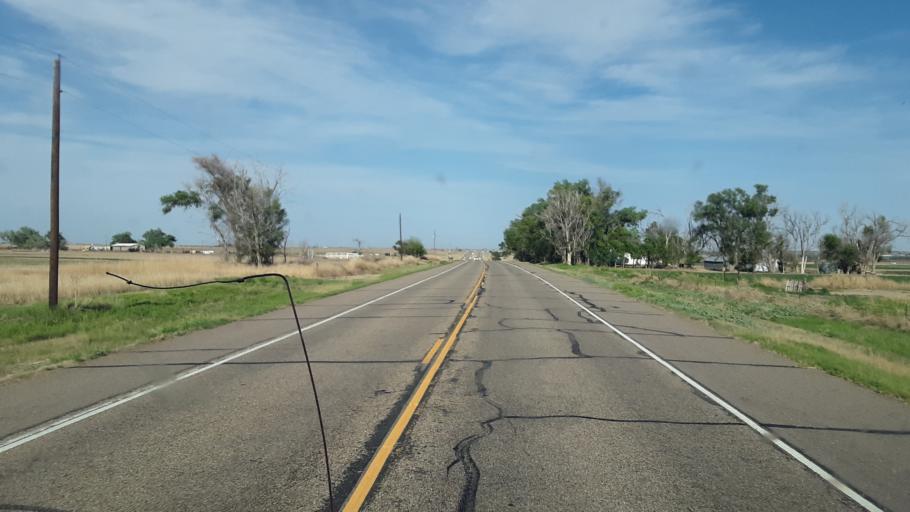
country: US
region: Colorado
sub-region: Prowers County
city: Lamar
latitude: 38.1142
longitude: -102.7522
